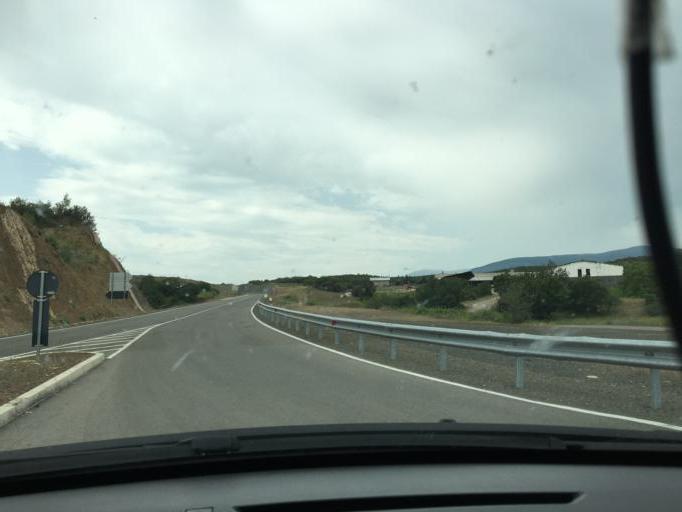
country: MK
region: Gevgelija
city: Miravci
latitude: 41.3040
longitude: 22.4435
